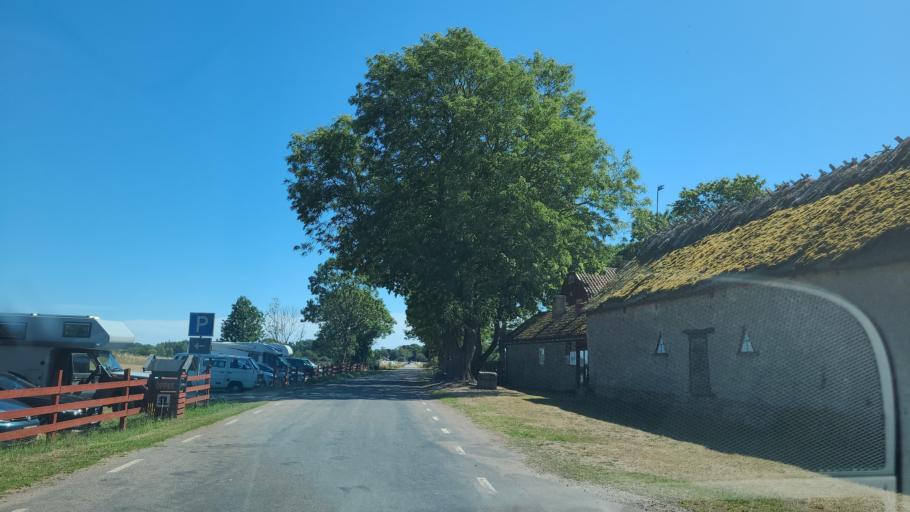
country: SE
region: Kalmar
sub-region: Borgholms Kommun
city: Borgholm
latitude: 56.7401
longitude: 16.7105
